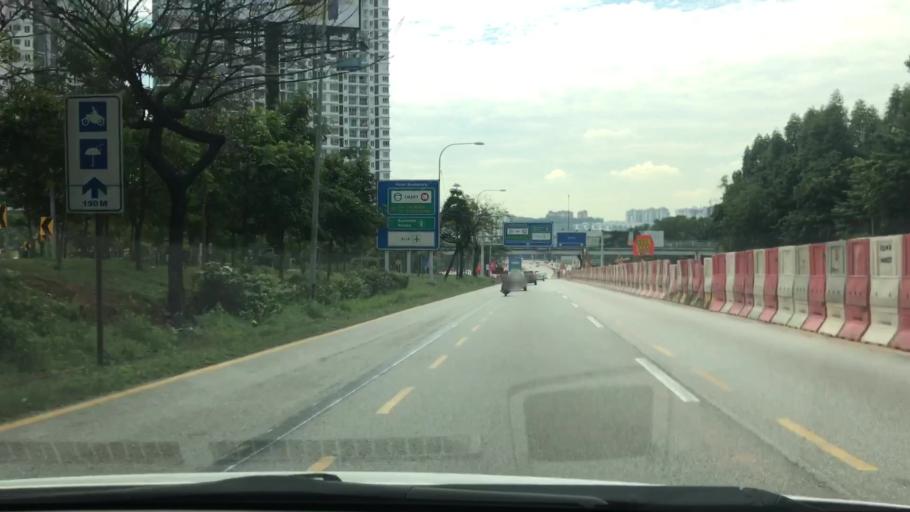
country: MY
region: Kuala Lumpur
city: Kuala Lumpur
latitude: 3.1070
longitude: 101.6929
